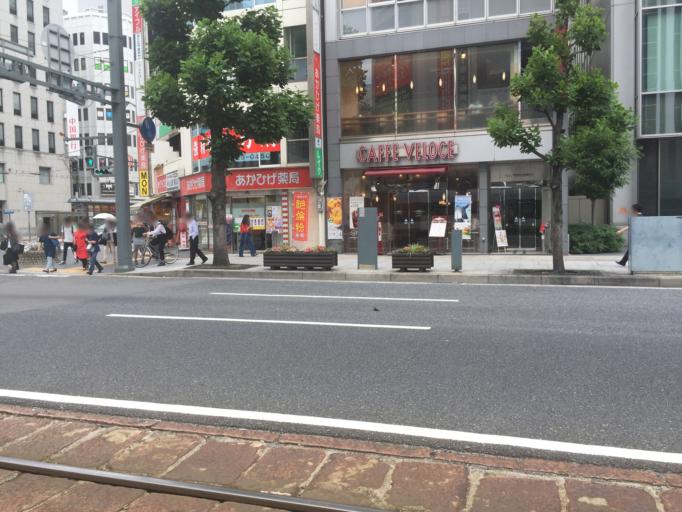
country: JP
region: Hiroshima
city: Hiroshima-shi
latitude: 34.3937
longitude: 132.4638
